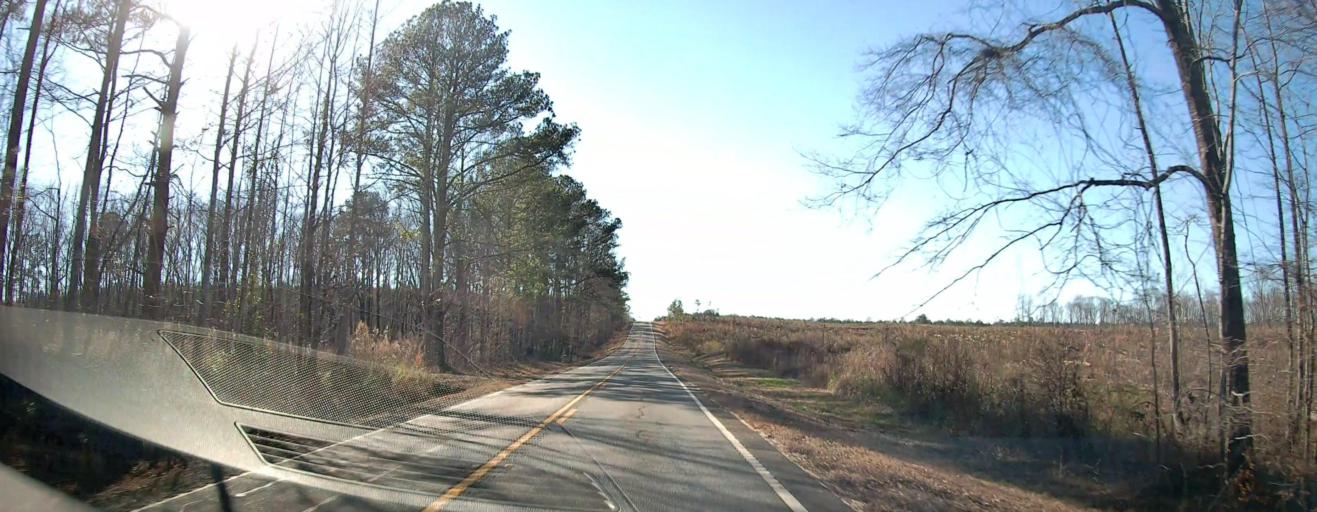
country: US
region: Georgia
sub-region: Talbot County
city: Talbotton
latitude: 32.6723
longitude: -84.4735
